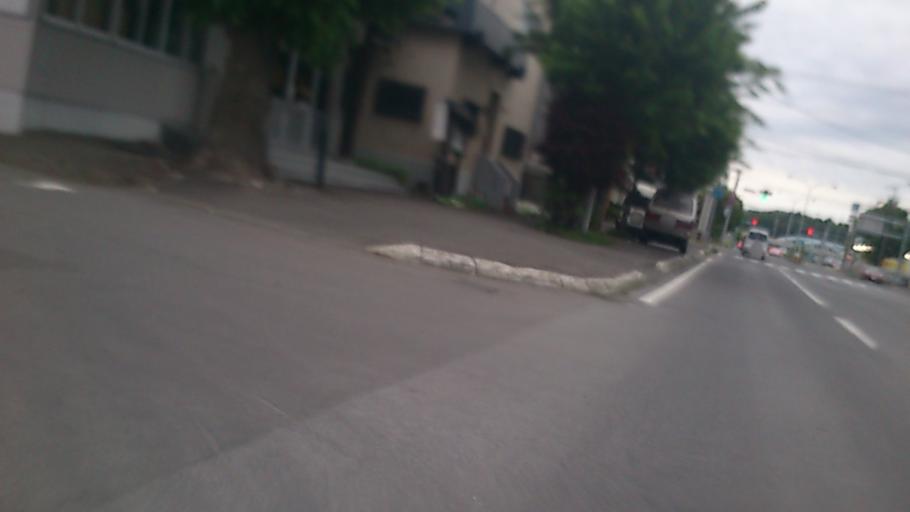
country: JP
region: Hokkaido
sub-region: Asahikawa-shi
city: Asahikawa
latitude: 43.7629
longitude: 142.3718
